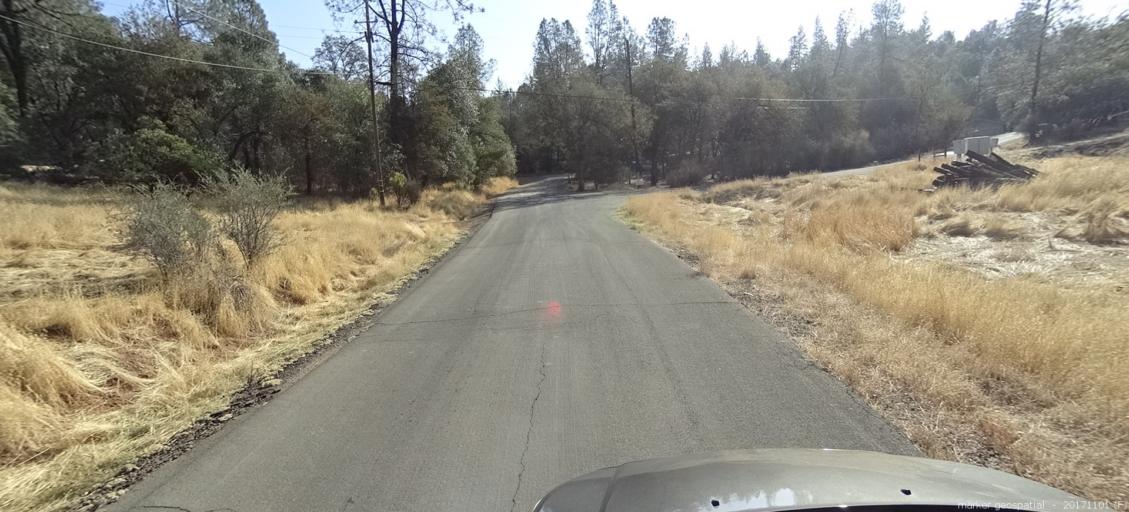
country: US
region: California
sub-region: Shasta County
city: Shasta Lake
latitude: 40.7077
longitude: -122.3207
